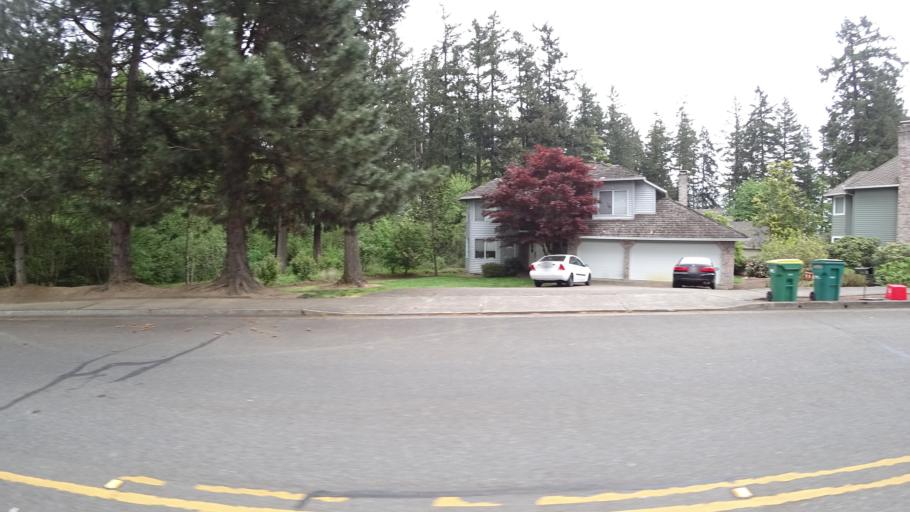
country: US
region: Oregon
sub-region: Washington County
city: Beaverton
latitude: 45.4600
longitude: -122.8206
